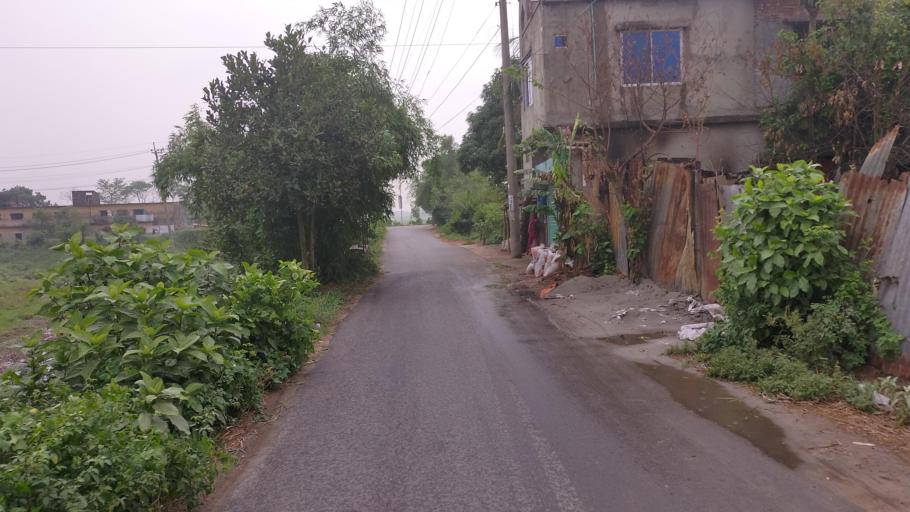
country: BD
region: Dhaka
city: Azimpur
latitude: 23.6837
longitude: 90.3504
